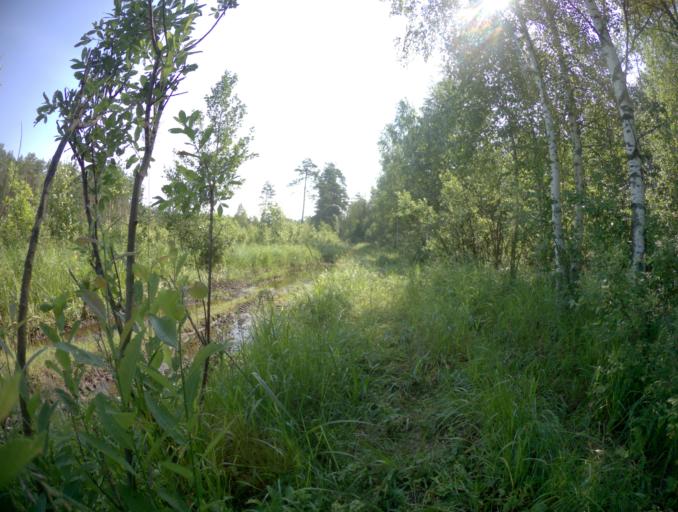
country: RU
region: Vladimir
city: Vyazniki
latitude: 56.3427
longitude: 42.1647
